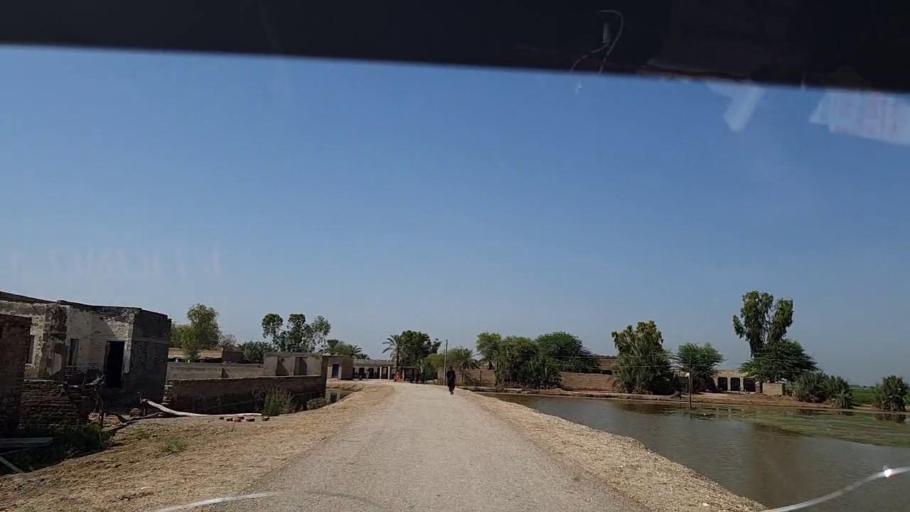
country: PK
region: Sindh
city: Tangwani
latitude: 28.3188
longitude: 69.0919
